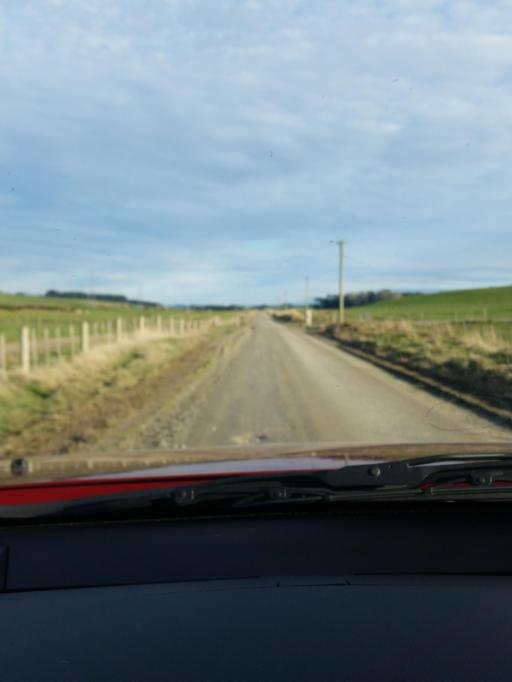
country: NZ
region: Southland
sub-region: Gore District
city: Gore
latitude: -46.2137
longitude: 168.7569
